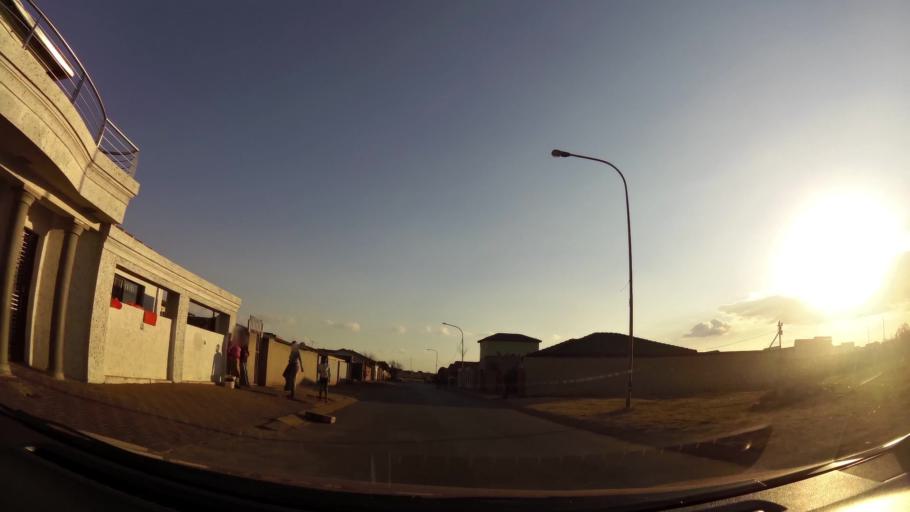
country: ZA
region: Gauteng
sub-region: City of Johannesburg Metropolitan Municipality
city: Soweto
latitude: -26.2242
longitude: 27.8554
